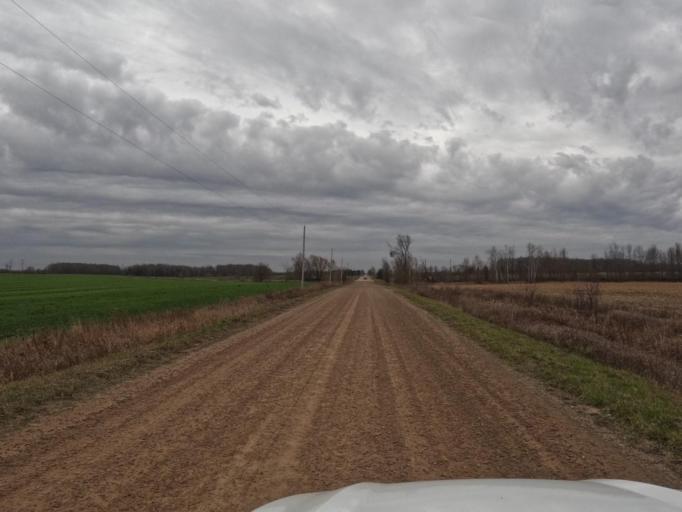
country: CA
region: Ontario
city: Shelburne
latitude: 43.9853
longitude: -80.3834
